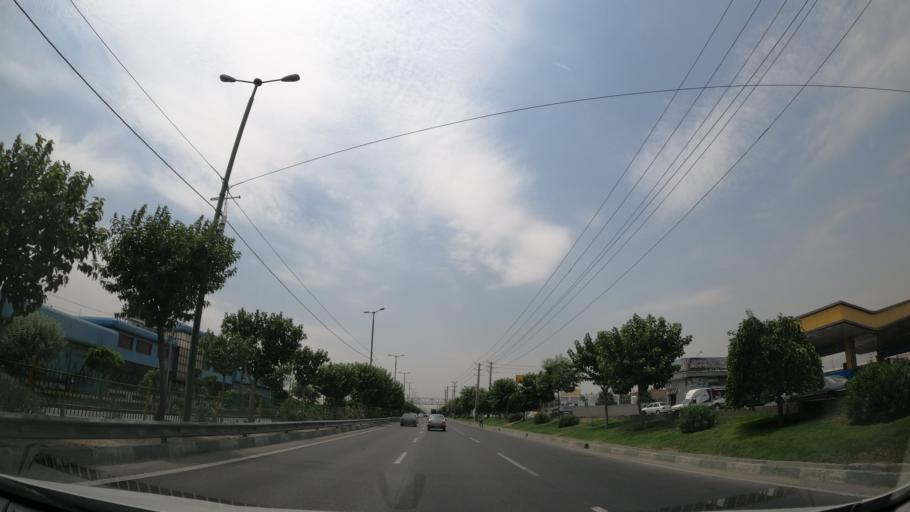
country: IR
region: Tehran
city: Tehran
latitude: 35.6764
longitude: 51.2908
